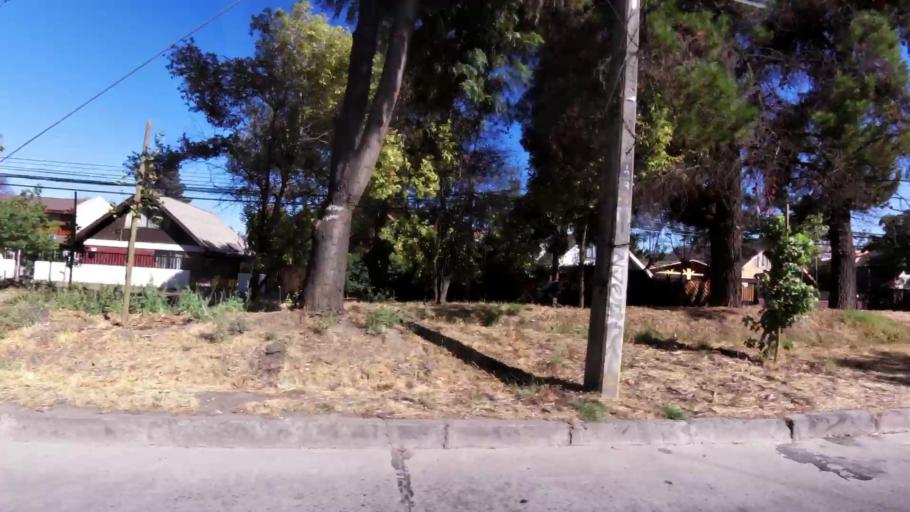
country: CL
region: O'Higgins
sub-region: Provincia de Cachapoal
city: Rancagua
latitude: -34.1820
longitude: -70.7187
